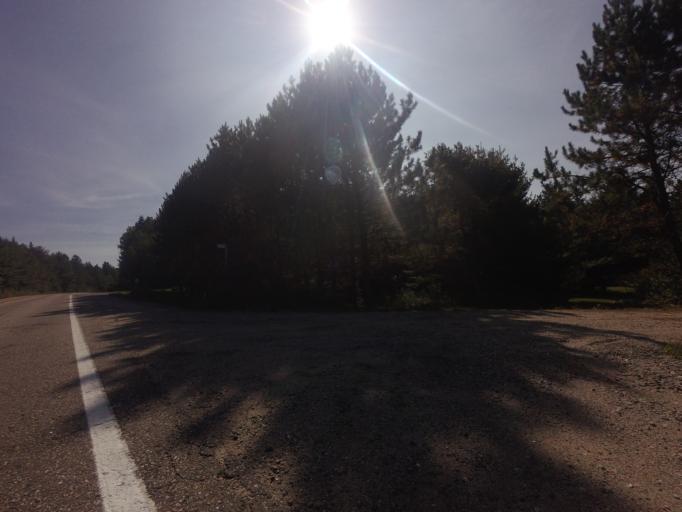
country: CA
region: Quebec
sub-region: Outaouais
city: Maniwaki
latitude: 46.4877
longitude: -75.8201
